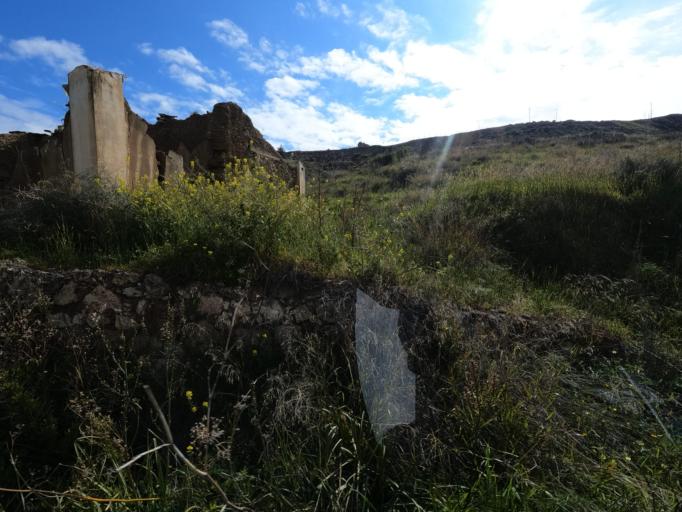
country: CY
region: Lefkosia
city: Lefka
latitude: 35.1011
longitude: 32.8863
